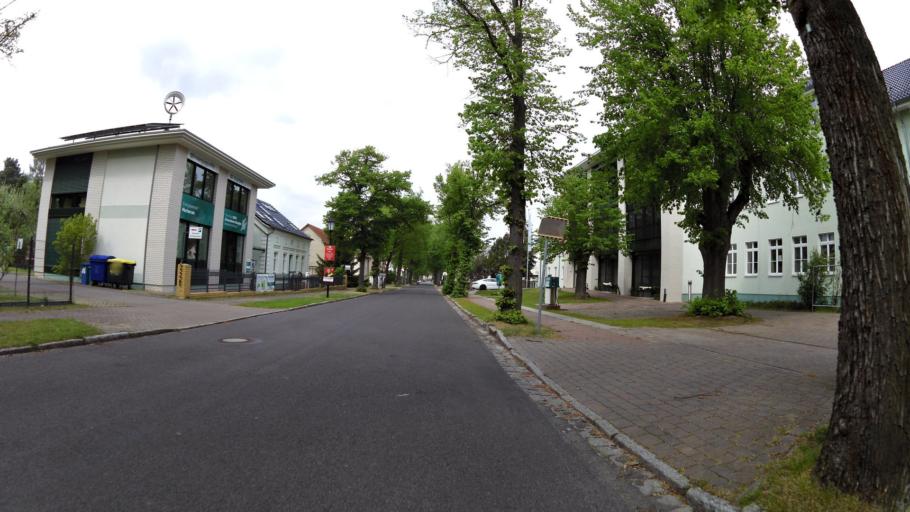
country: DE
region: Brandenburg
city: Mittenwalde
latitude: 52.2093
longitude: 13.5622
